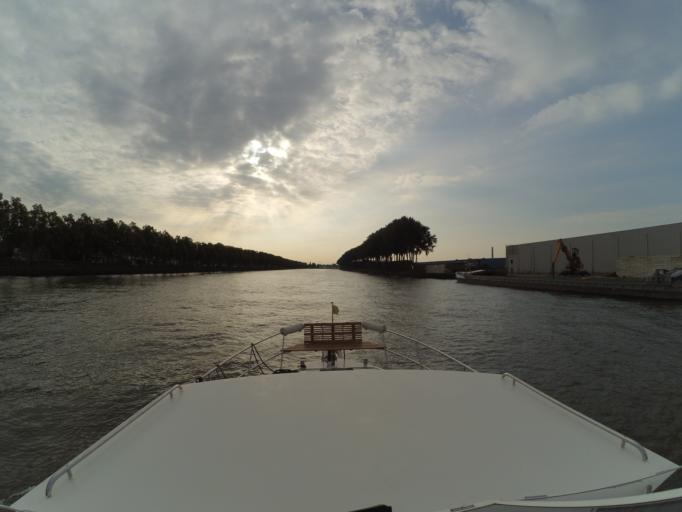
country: NL
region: Utrecht
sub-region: Stichtse Vecht
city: Maarssen
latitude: 52.1199
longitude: 5.0652
